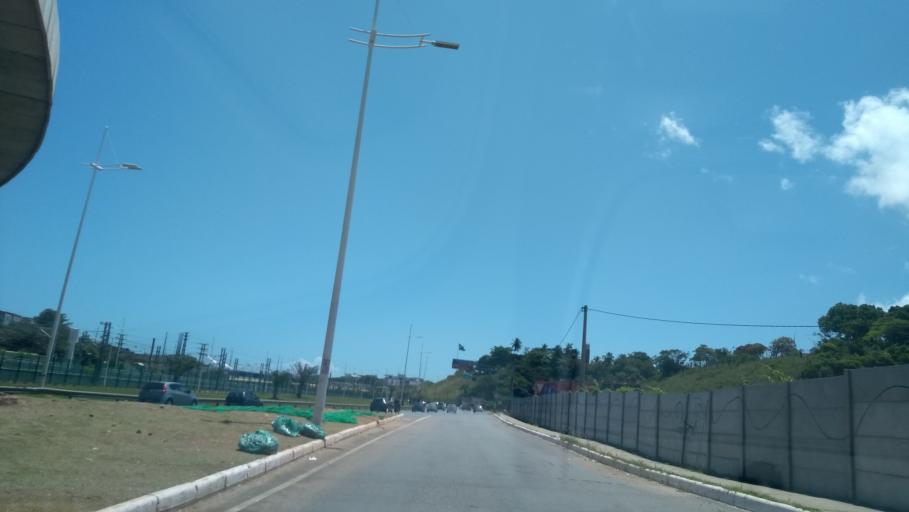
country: BR
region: Bahia
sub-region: Lauro De Freitas
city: Lauro de Freitas
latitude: -12.9393
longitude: -38.4162
